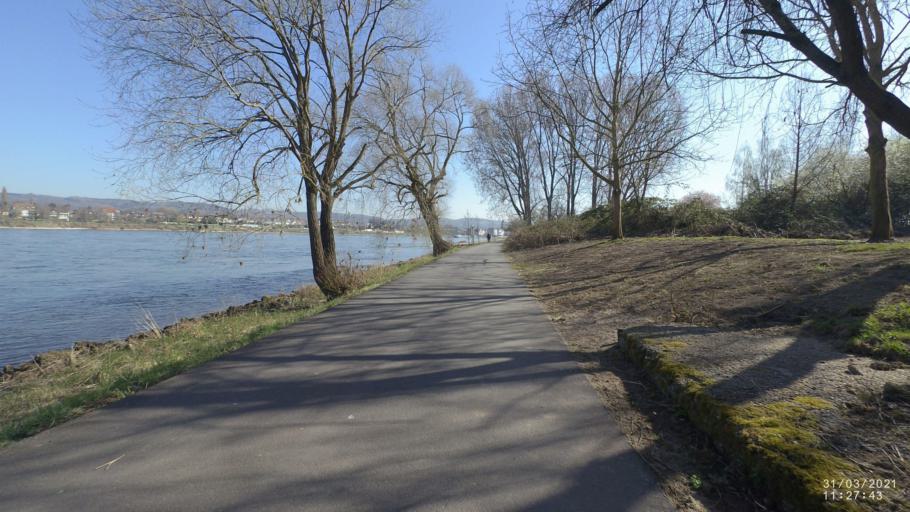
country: DE
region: Rheinland-Pfalz
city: Urmitz
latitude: 50.4198
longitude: 7.5266
